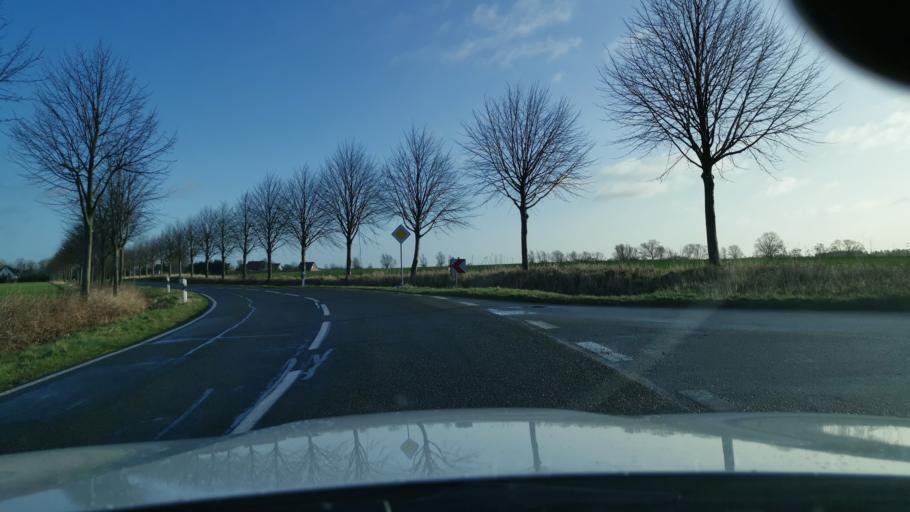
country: DE
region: Mecklenburg-Vorpommern
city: Laage
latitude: 53.9813
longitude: 12.3502
